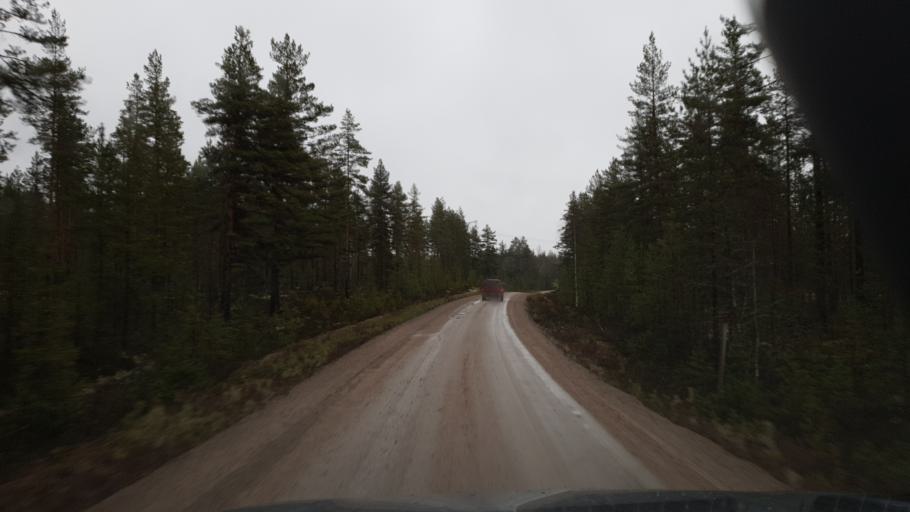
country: SE
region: Vaesternorrland
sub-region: Ange Kommun
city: Ange
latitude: 62.2077
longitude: 15.5452
